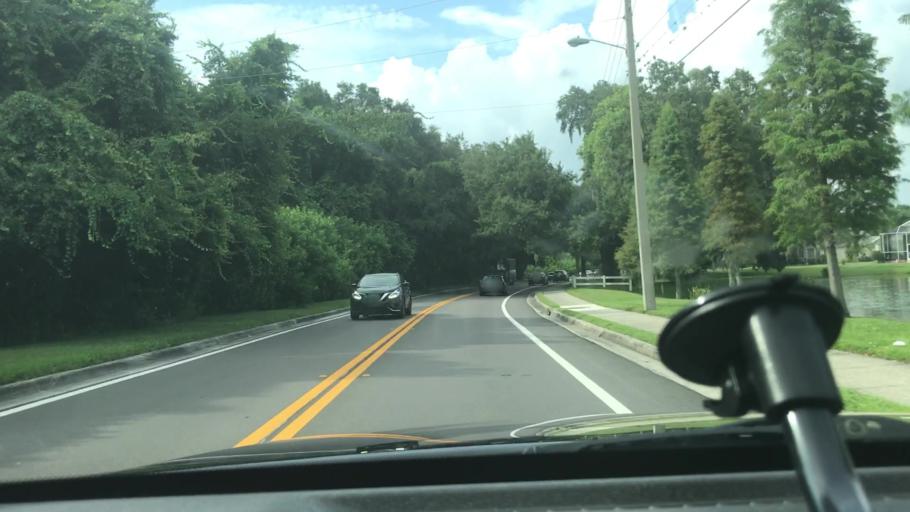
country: US
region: Florida
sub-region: Hillsborough County
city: Progress Village
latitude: 27.9064
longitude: -82.3306
